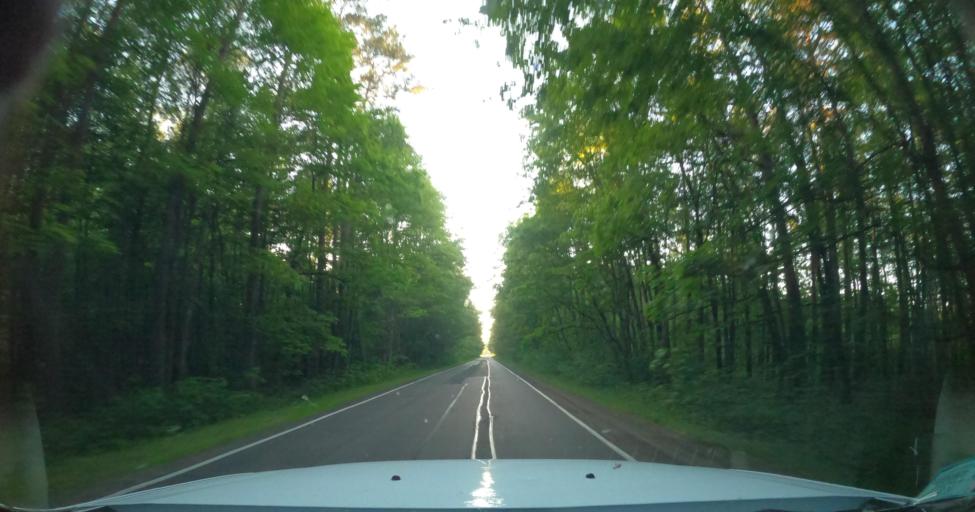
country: PL
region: Pomeranian Voivodeship
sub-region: Powiat bytowski
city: Czarna Dabrowka
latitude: 54.3815
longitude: 17.4875
